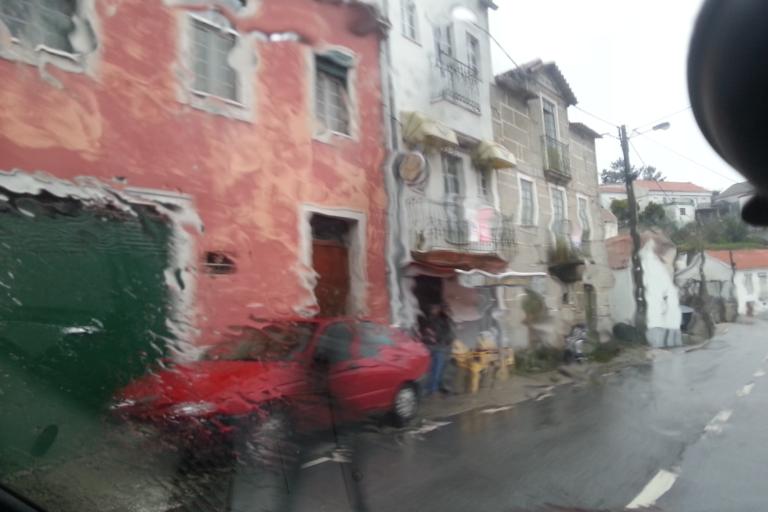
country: PT
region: Guarda
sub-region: Fornos de Algodres
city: Fornos de Algodres
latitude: 40.5170
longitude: -7.5815
